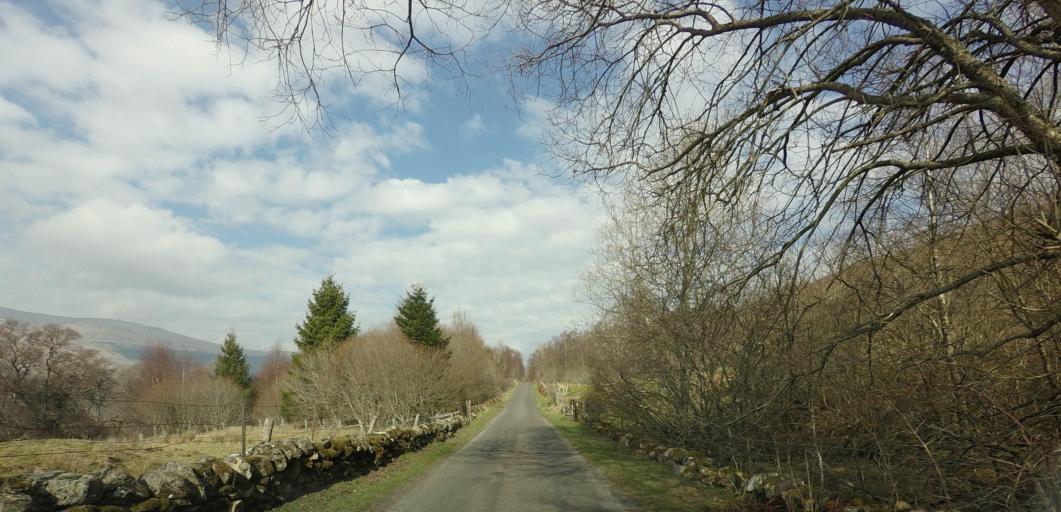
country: GB
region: Scotland
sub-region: Perth and Kinross
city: Comrie
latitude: 56.5319
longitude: -4.1083
